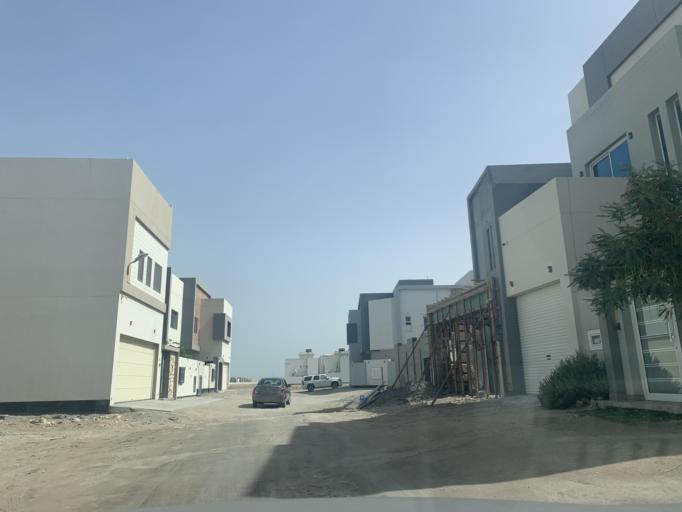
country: BH
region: Northern
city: Sitrah
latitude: 26.1695
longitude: 50.6290
